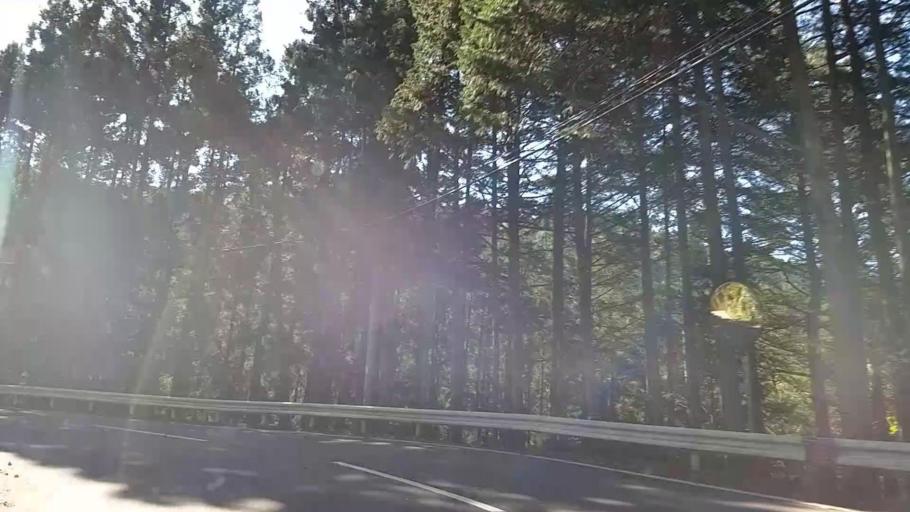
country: JP
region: Yamanashi
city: Otsuki
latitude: 35.7489
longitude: 138.9601
